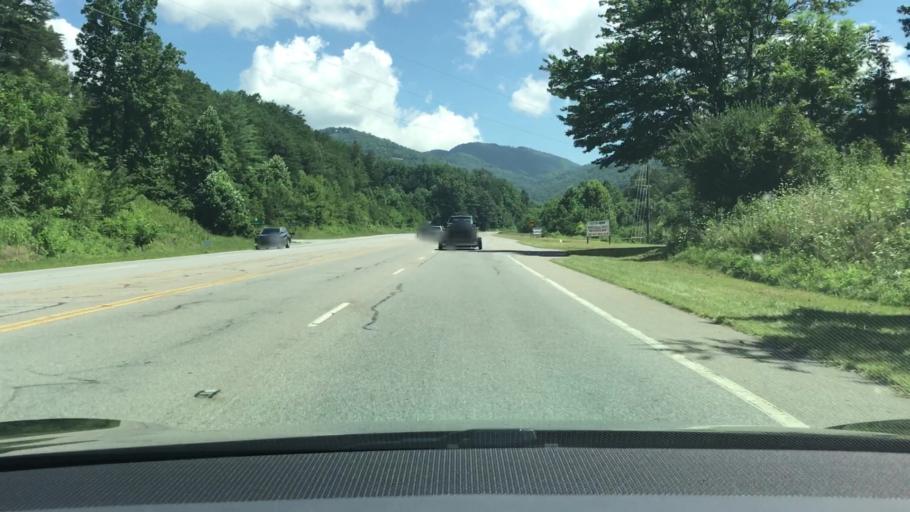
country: US
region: North Carolina
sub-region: Macon County
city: Franklin
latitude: 35.2296
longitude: -83.3503
